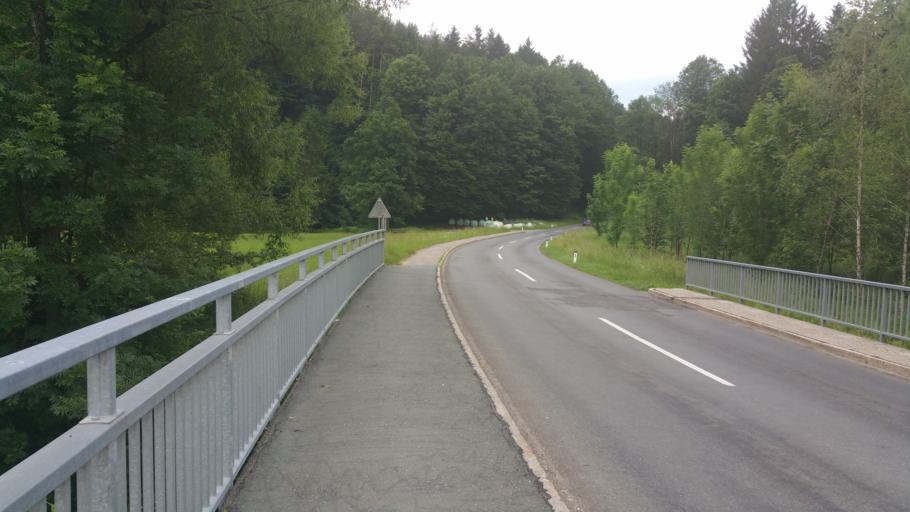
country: AT
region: Styria
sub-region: Politischer Bezirk Deutschlandsberg
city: Sankt Martin im Sulmtal
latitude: 46.7347
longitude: 15.3264
